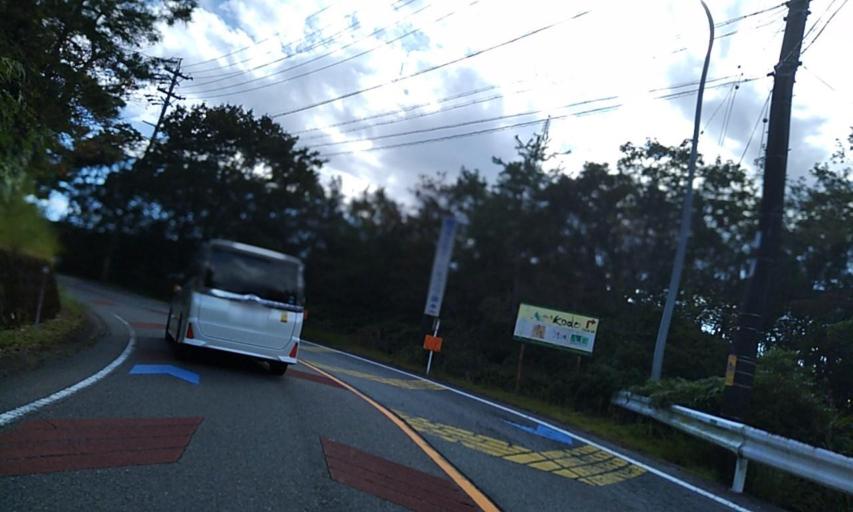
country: JP
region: Mie
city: Owase
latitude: 34.2097
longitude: 136.3529
